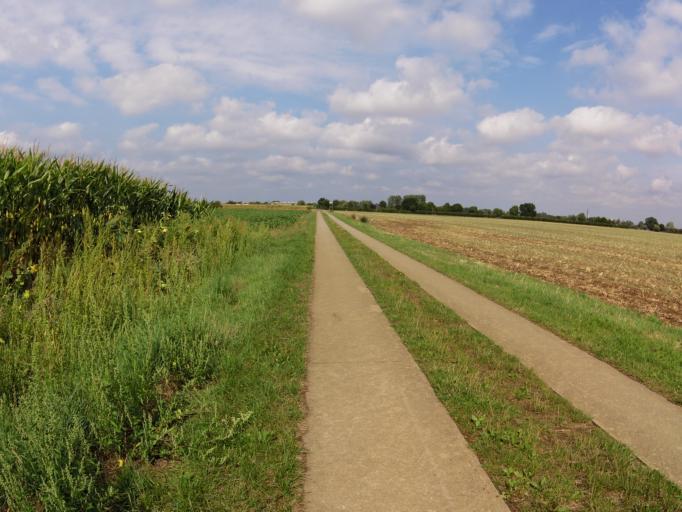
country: DE
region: Lower Saxony
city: Bucken
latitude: 52.7889
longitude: 9.1417
